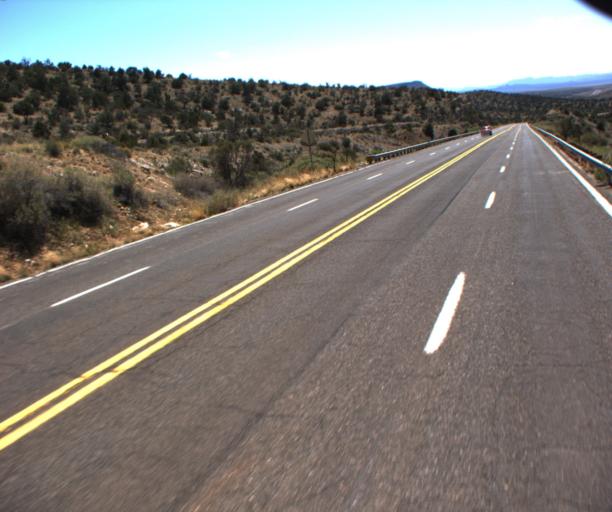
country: US
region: Arizona
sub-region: Mohave County
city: Peach Springs
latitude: 35.5465
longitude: -113.3987
